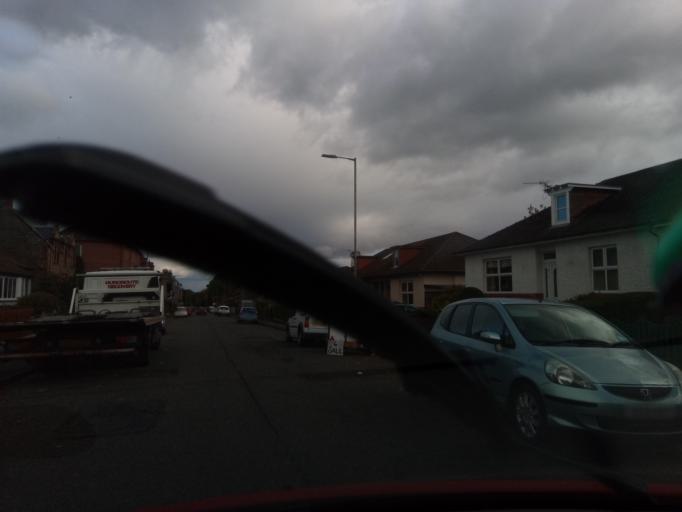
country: GB
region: Scotland
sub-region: The Scottish Borders
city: Galashiels
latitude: 55.6083
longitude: -2.7947
